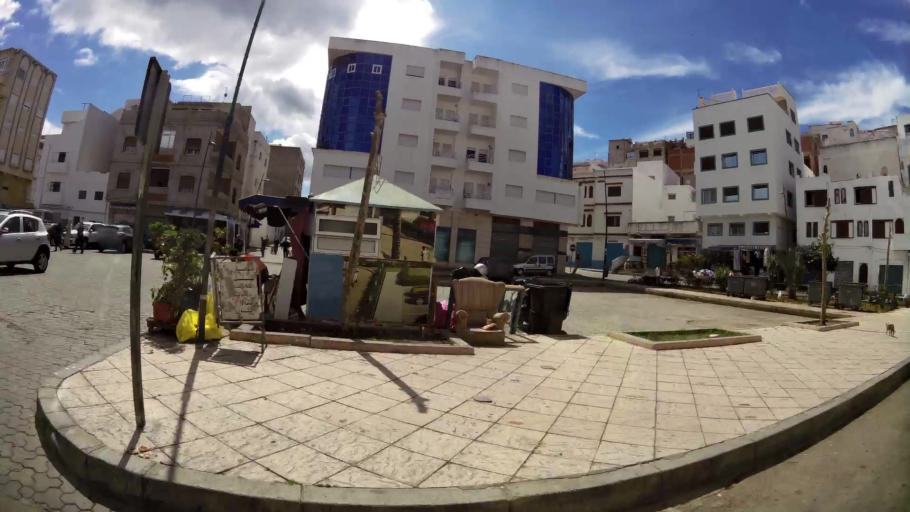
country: MA
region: Tanger-Tetouan
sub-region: Tetouan
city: Martil
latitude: 35.6830
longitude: -5.3225
